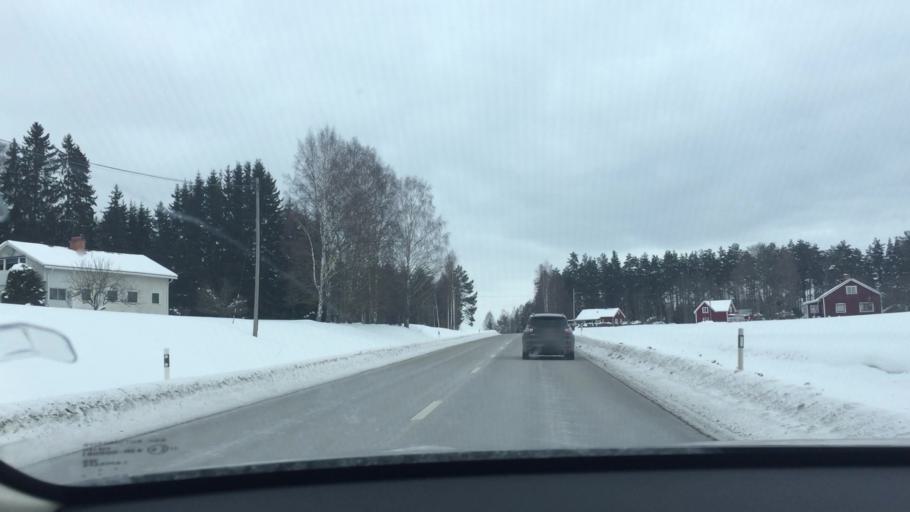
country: SE
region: Dalarna
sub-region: Faluns Kommun
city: Svardsjo
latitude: 60.6360
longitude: 15.8370
